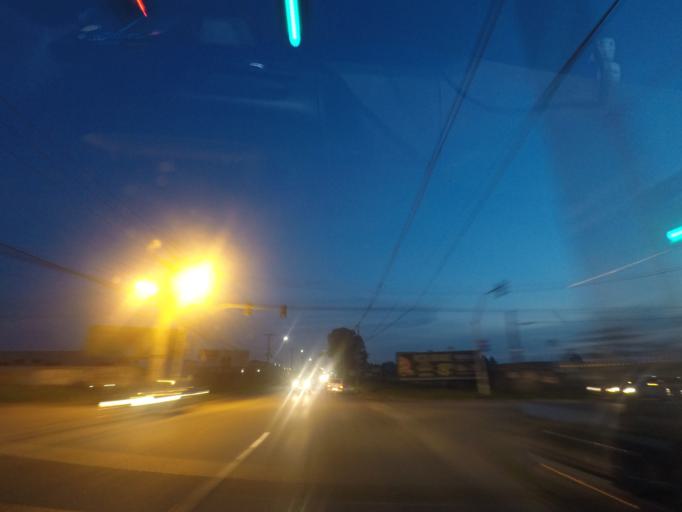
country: BR
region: Parana
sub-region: Pinhais
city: Pinhais
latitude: -25.4882
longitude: -49.1559
